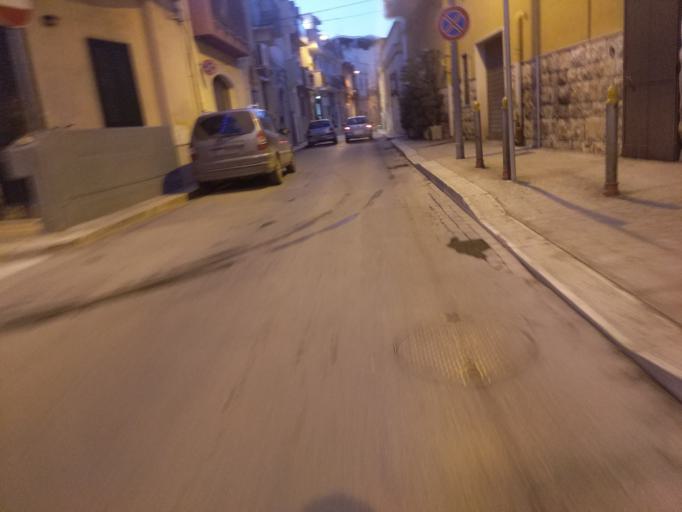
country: IT
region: Apulia
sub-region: Provincia di Bari
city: Modugno
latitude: 41.0807
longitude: 16.7791
